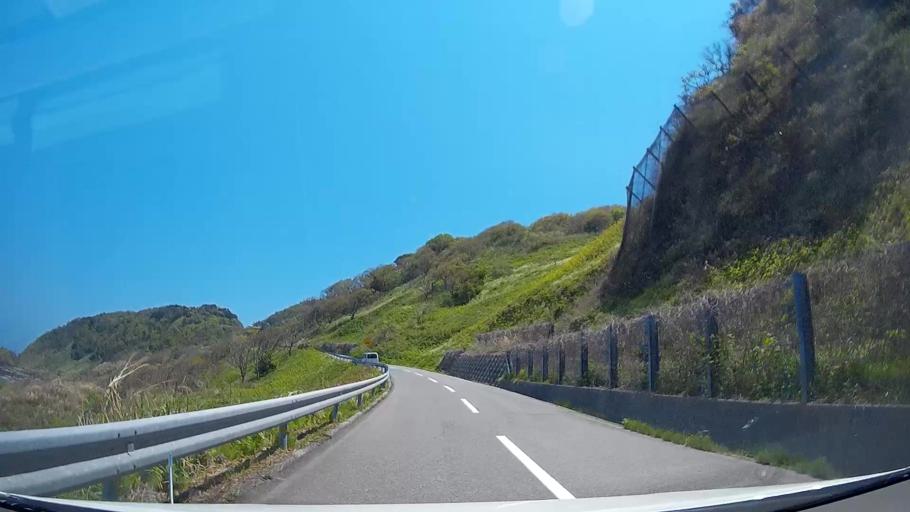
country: JP
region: Ishikawa
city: Nanao
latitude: 37.5242
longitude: 137.2502
